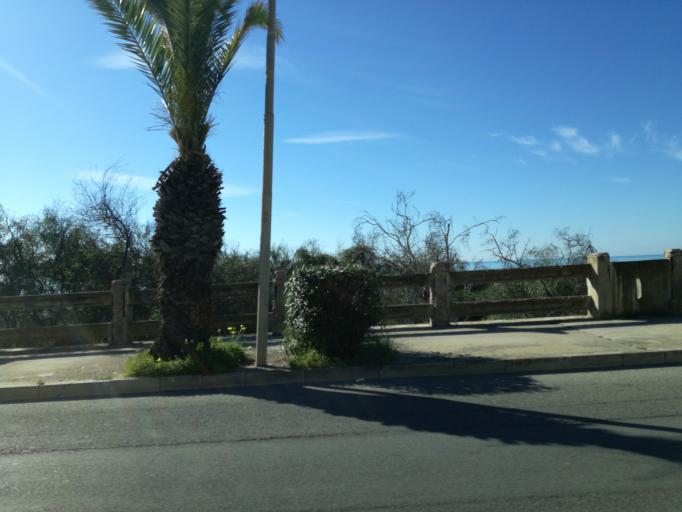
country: IT
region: Sicily
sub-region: Provincia di Caltanissetta
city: Gela
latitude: 37.0716
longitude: 14.2204
